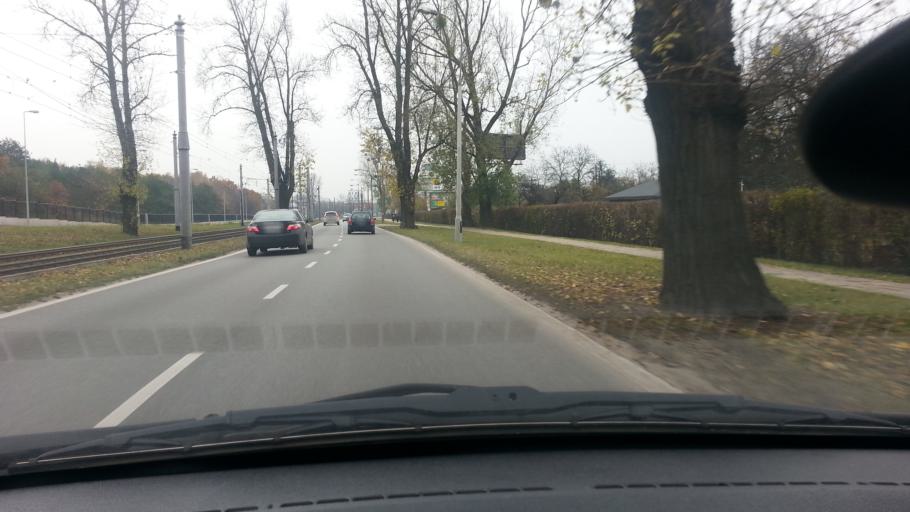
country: PL
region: Masovian Voivodeship
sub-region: Warszawa
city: Praga Polnoc
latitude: 52.2725
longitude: 21.0329
